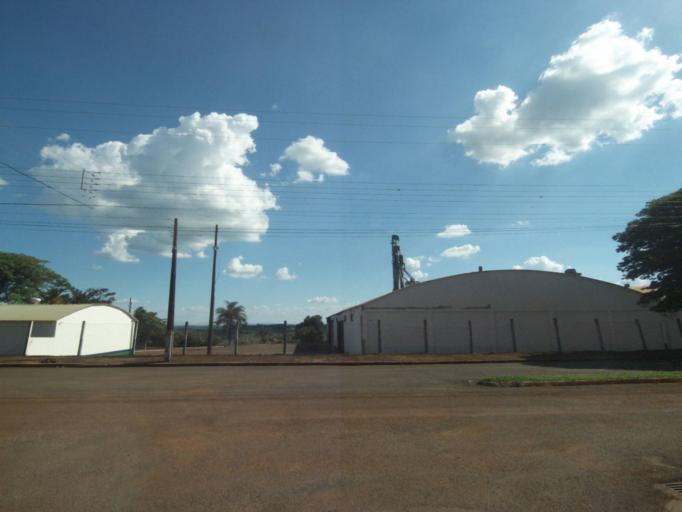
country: BR
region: Parana
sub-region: Sertanopolis
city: Sertanopolis
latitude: -23.0425
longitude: -50.8151
